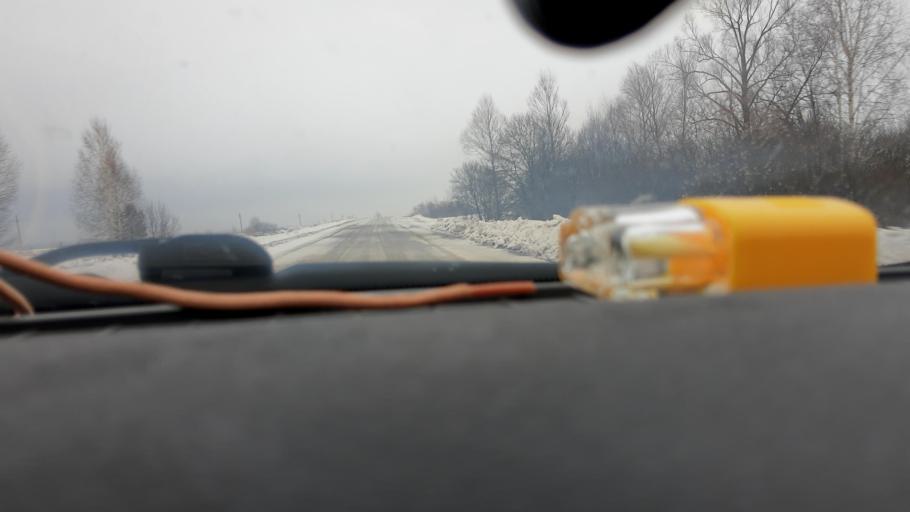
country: RU
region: Bashkortostan
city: Iglino
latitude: 54.6301
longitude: 56.4258
